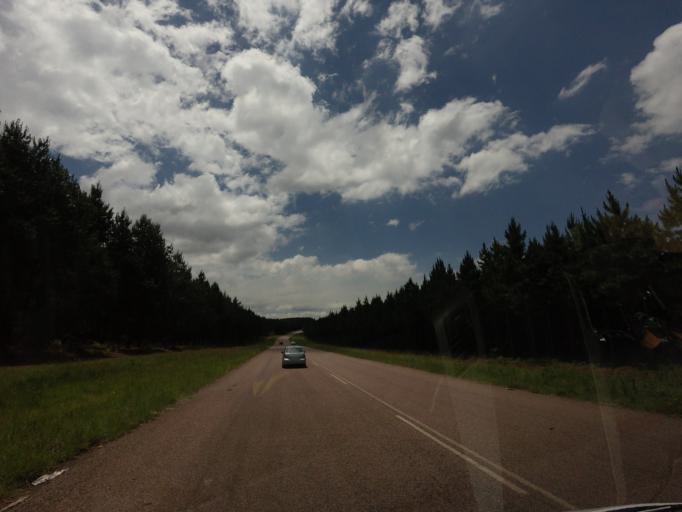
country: ZA
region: Mpumalanga
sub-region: Ehlanzeni District
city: Graksop
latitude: -25.0338
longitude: 30.8206
